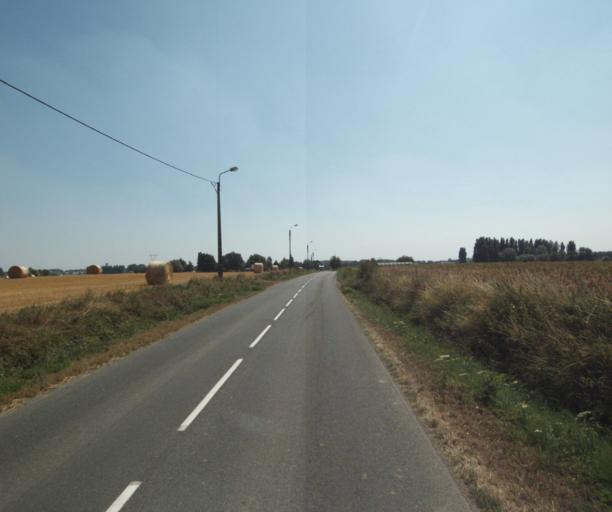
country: FR
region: Nord-Pas-de-Calais
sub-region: Departement du Nord
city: Linselles
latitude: 50.7496
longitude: 3.0561
